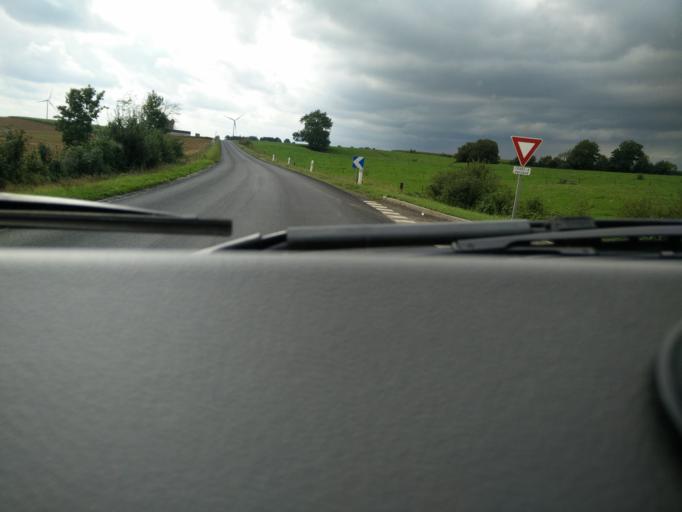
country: FR
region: Champagne-Ardenne
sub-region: Departement des Ardennes
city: Signy-le-Petit
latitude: 49.8716
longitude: 4.3122
